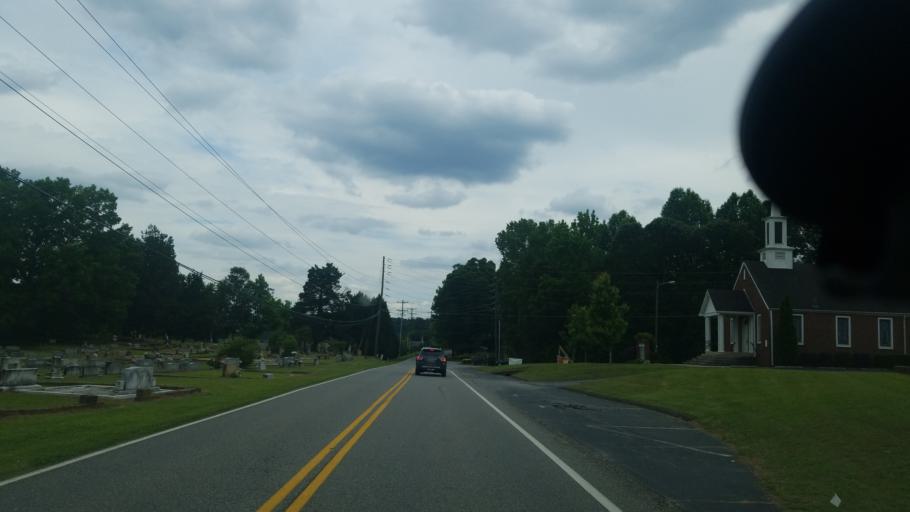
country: US
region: Georgia
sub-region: Forsyth County
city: Cumming
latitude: 34.1719
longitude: -84.1273
